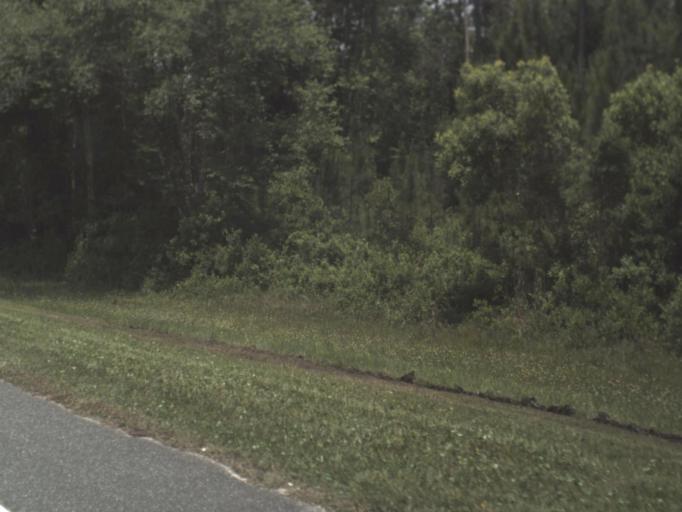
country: US
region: Florida
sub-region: Columbia County
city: Watertown
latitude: 30.1152
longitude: -82.5018
